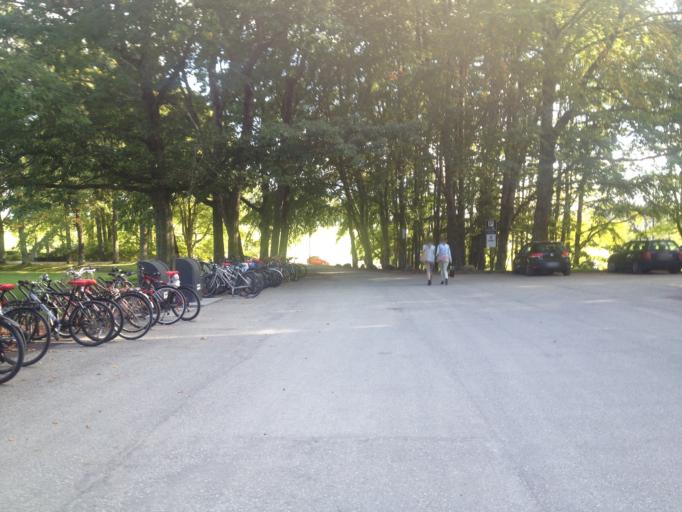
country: NO
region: Akershus
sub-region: As
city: As
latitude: 59.6653
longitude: 10.7657
